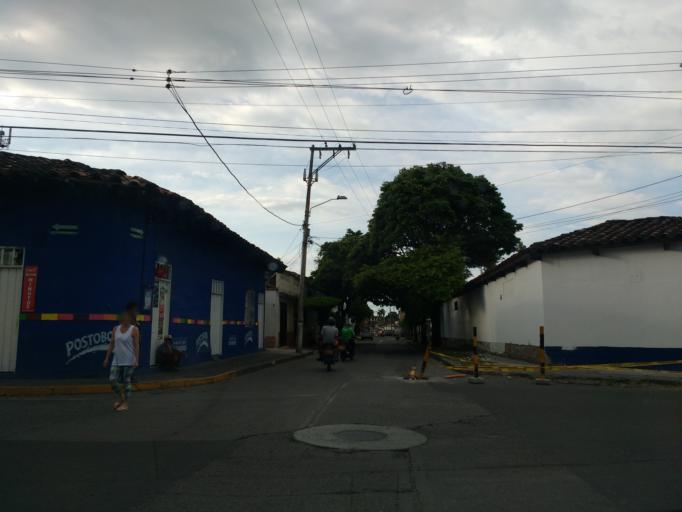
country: CO
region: Valle del Cauca
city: Cartago
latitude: 4.7478
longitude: -75.9198
